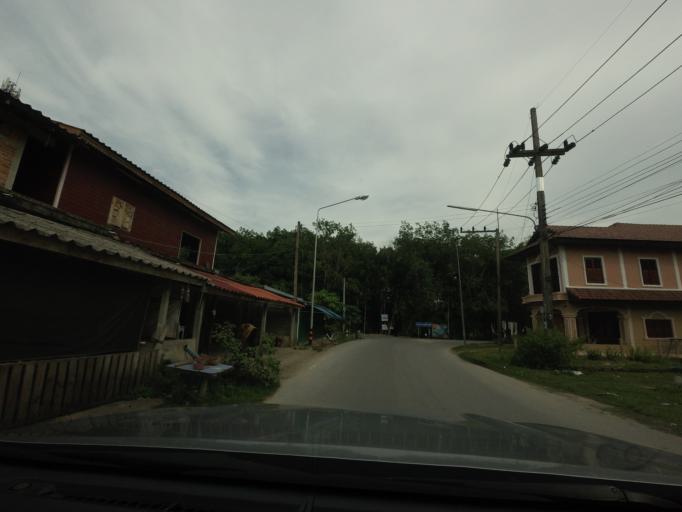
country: TH
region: Yala
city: Raman
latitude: 6.4387
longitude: 101.4554
